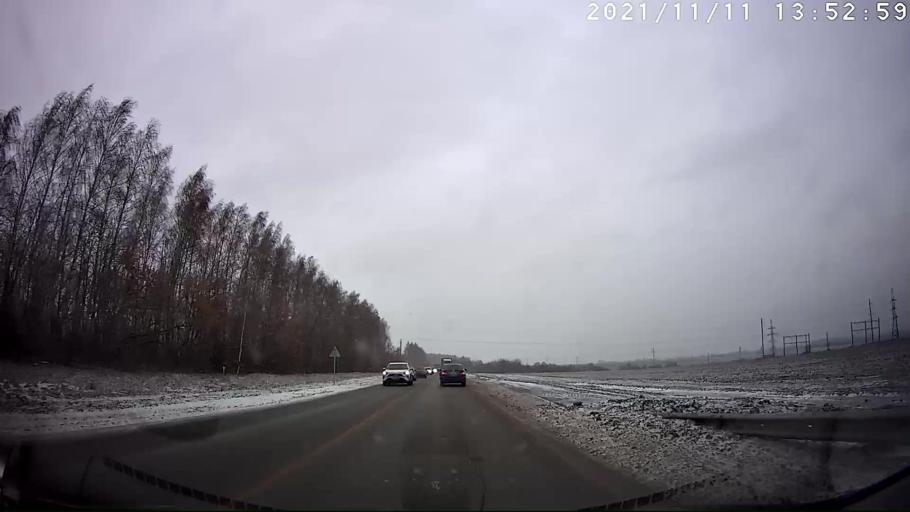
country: RU
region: Chuvashia
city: Shikhazany
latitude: 55.5736
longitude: 47.4125
